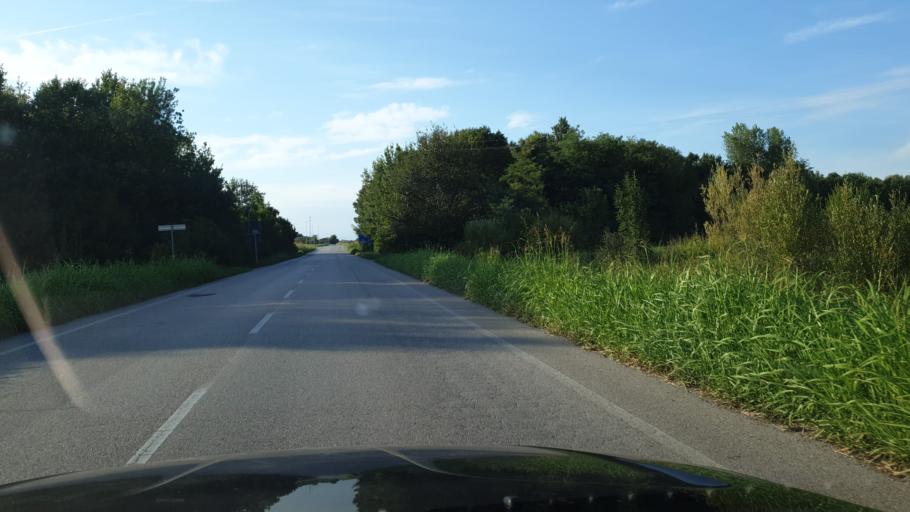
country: IT
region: Veneto
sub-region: Provincia di Rovigo
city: Fiesso Umbertiano
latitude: 44.9627
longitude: 11.6143
